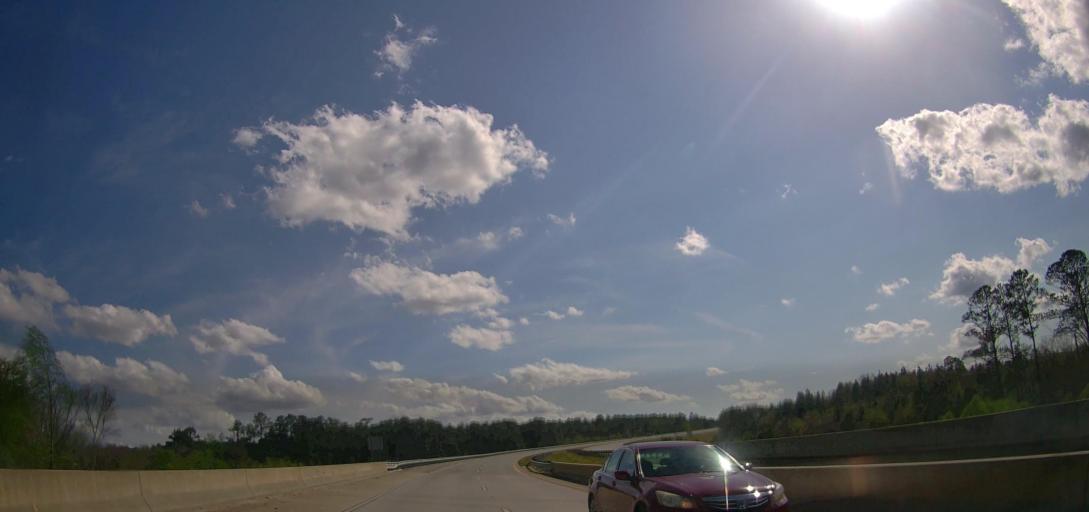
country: US
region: Georgia
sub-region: Baldwin County
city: Hardwick
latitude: 32.9841
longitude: -83.2063
